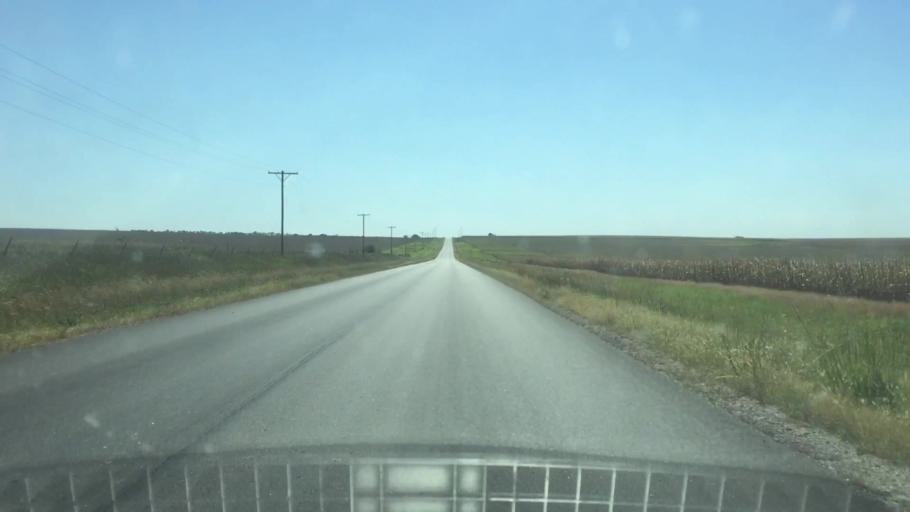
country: US
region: Kansas
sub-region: Marshall County
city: Marysville
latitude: 39.9168
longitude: -96.6009
